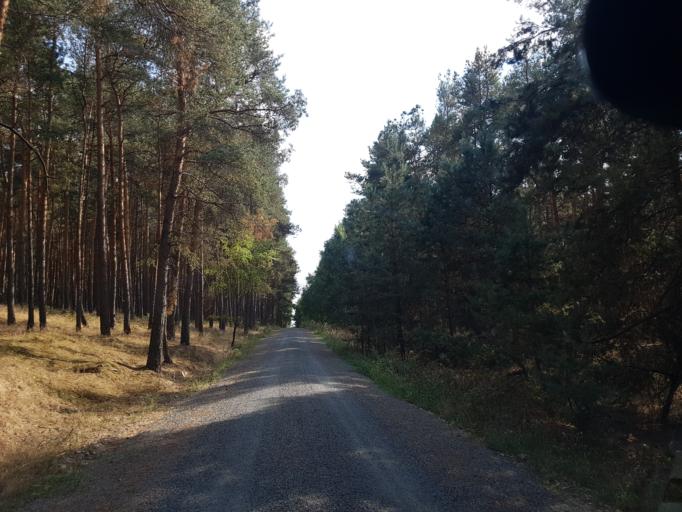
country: DE
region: Brandenburg
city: Treuenbrietzen
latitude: 52.0160
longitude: 12.8625
